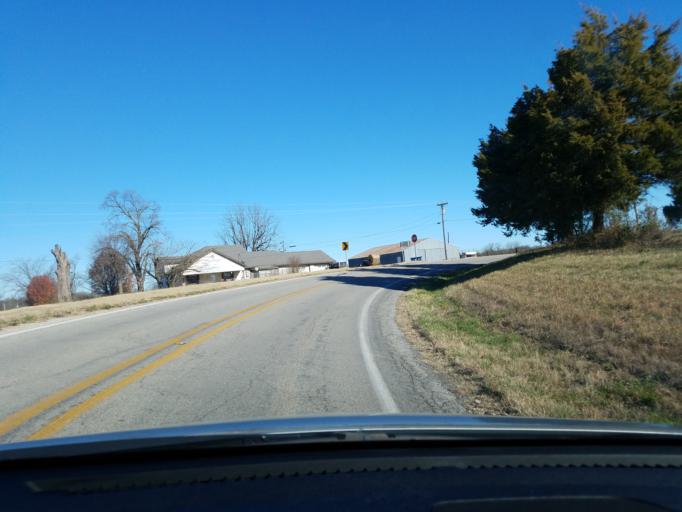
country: US
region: Arkansas
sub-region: Carroll County
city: Green Forest
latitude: 36.4776
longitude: -93.4268
